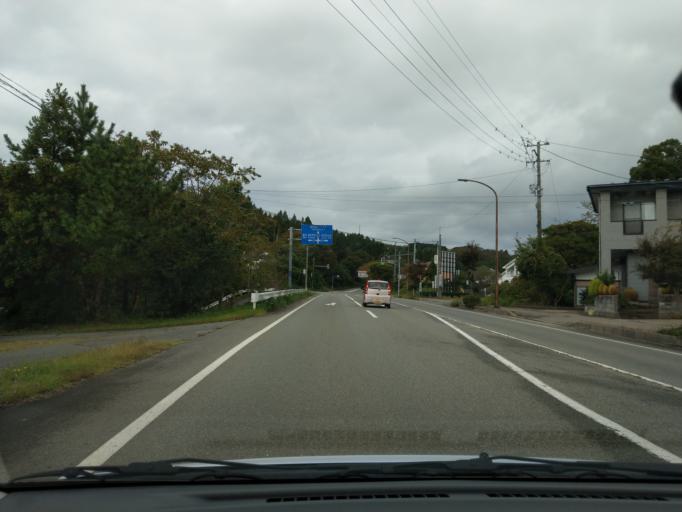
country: JP
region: Akita
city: Akita Shi
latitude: 39.6702
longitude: 140.0835
